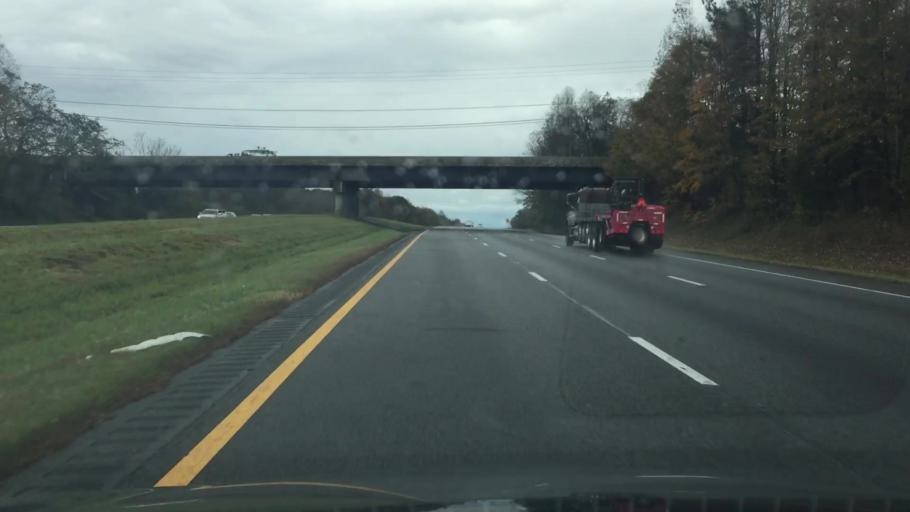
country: US
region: North Carolina
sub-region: Davidson County
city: Thomasville
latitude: 35.8649
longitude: -80.0370
